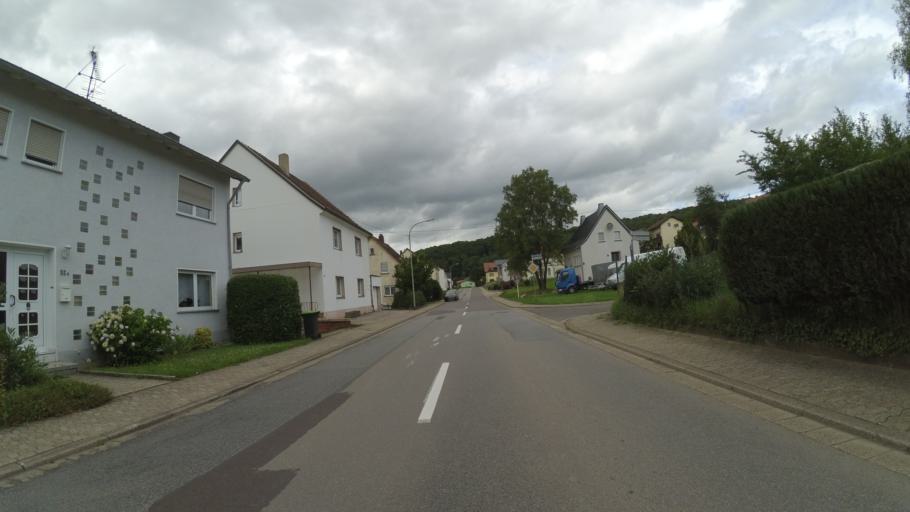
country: DE
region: Saarland
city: Tholey
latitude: 49.4689
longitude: 7.0009
